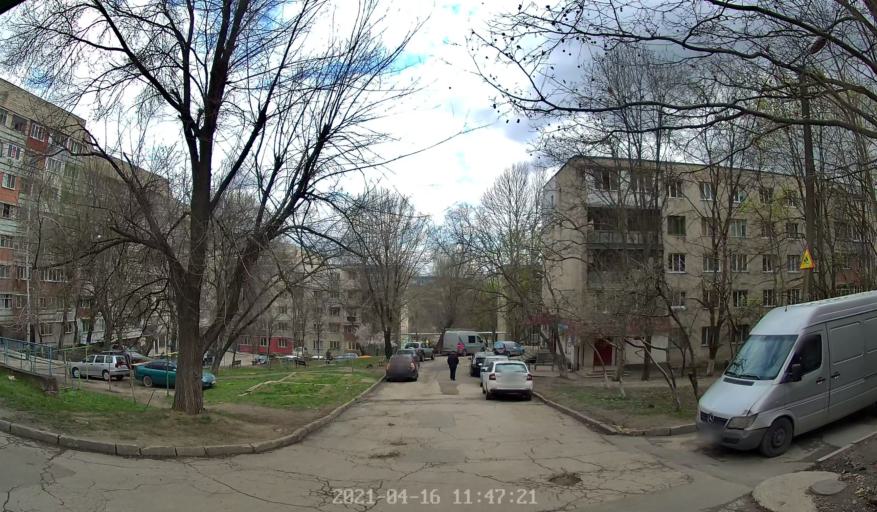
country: MD
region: Chisinau
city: Stauceni
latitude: 47.0605
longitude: 28.8418
